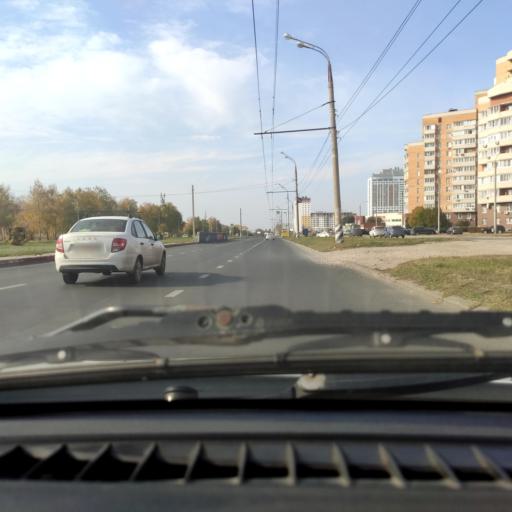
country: RU
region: Samara
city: Tol'yatti
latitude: 53.4991
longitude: 49.2819
